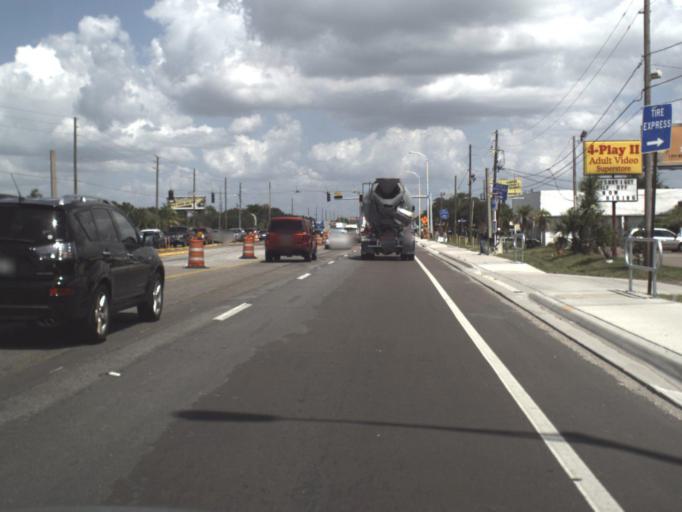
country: US
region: Florida
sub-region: Pinellas County
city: South Highpoint
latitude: 27.8941
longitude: -82.7450
